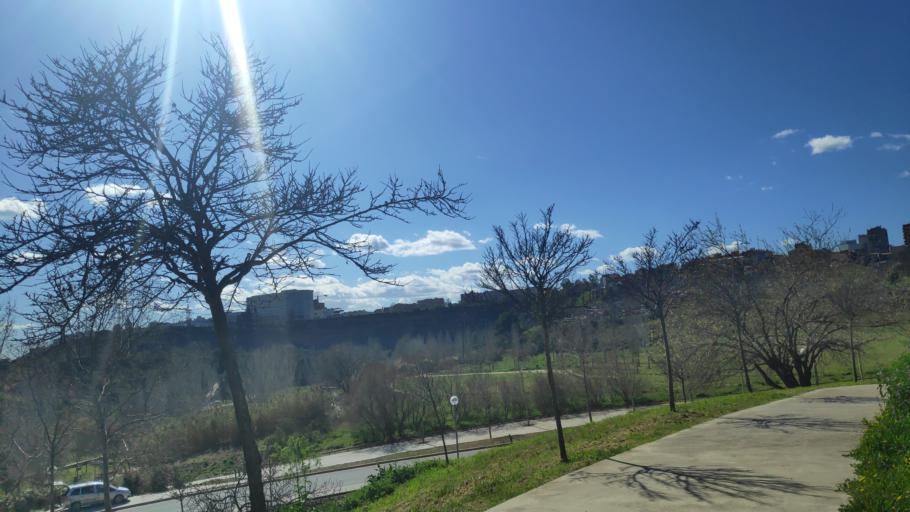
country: ES
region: Catalonia
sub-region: Provincia de Barcelona
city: Sabadell
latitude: 41.5649
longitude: 2.1087
